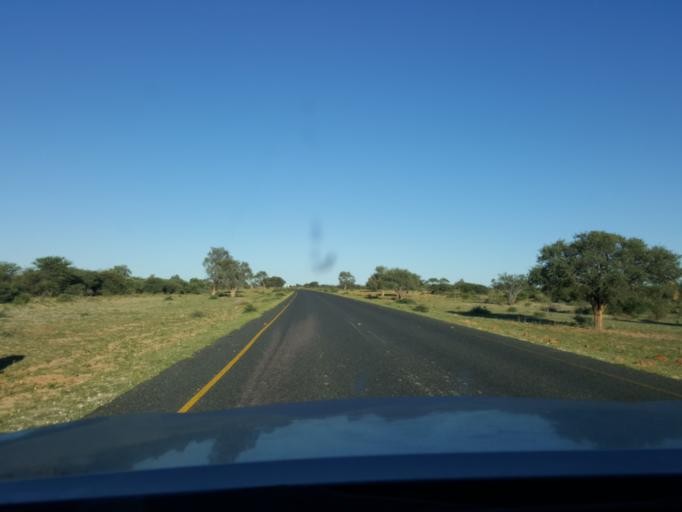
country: BW
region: Southern
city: Khakhea
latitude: -24.2550
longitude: 23.3010
